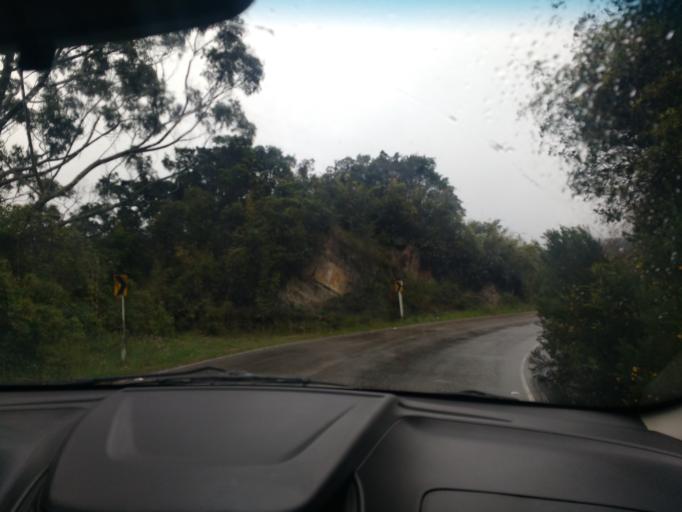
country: CO
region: Bogota D.C.
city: Bogota
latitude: 4.5880
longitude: -74.0462
